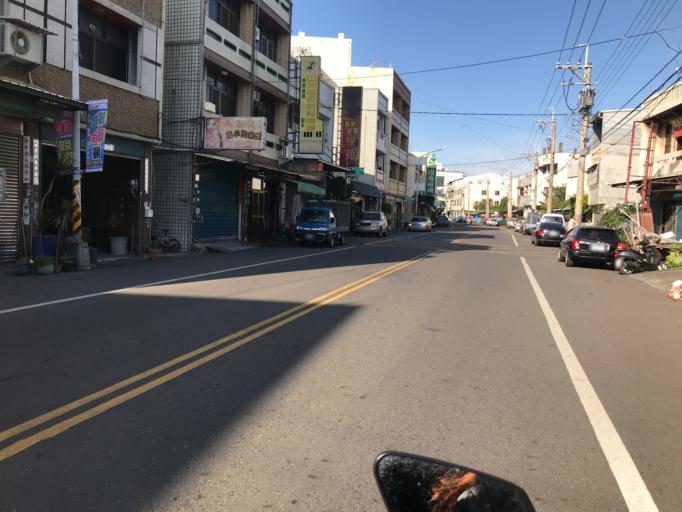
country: TW
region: Taiwan
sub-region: Nantou
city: Nantou
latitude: 23.8927
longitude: 120.5876
